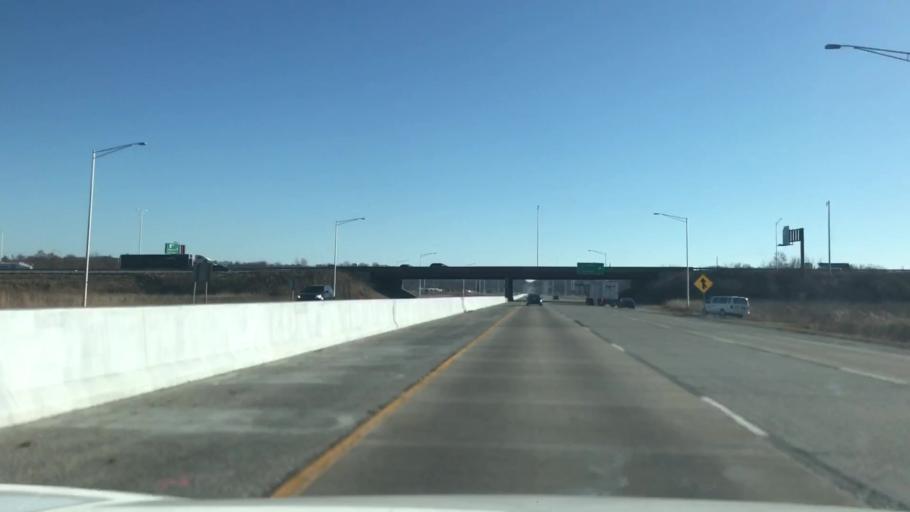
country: US
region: Illinois
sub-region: Saint Clair County
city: Alorton
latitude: 38.5838
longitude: -90.1094
